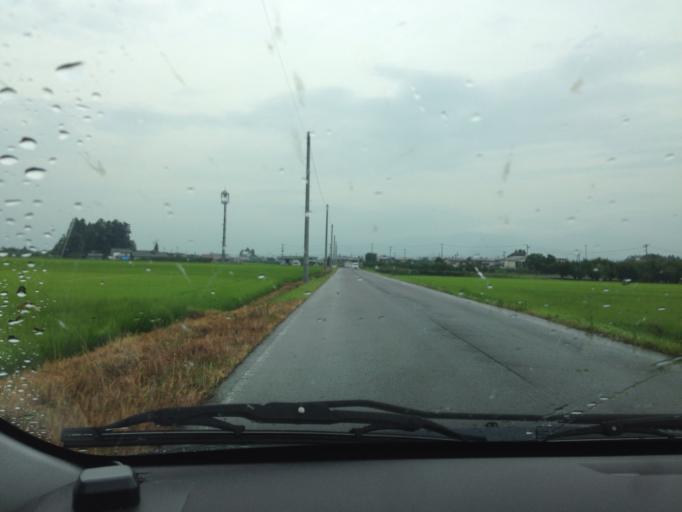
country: JP
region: Fukushima
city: Kitakata
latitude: 37.4518
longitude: 139.8305
